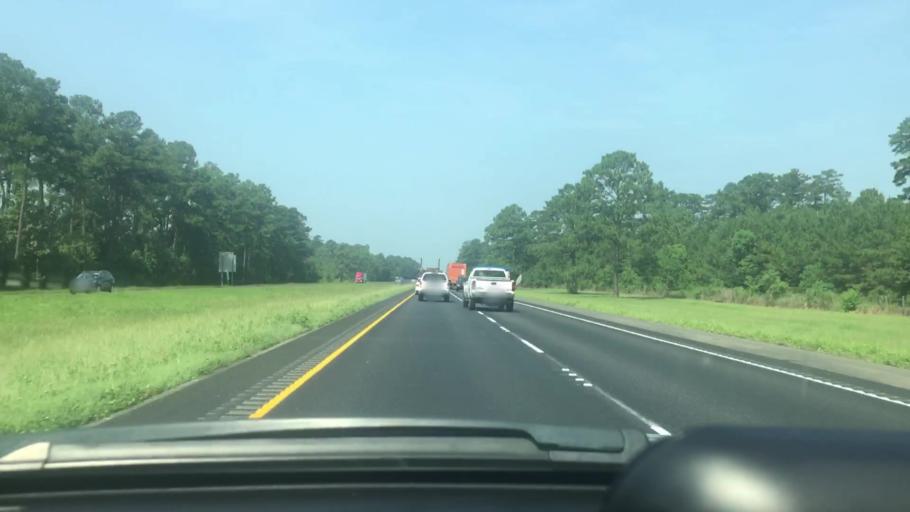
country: US
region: Louisiana
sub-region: Livingston Parish
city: Albany
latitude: 30.4747
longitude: -90.6613
